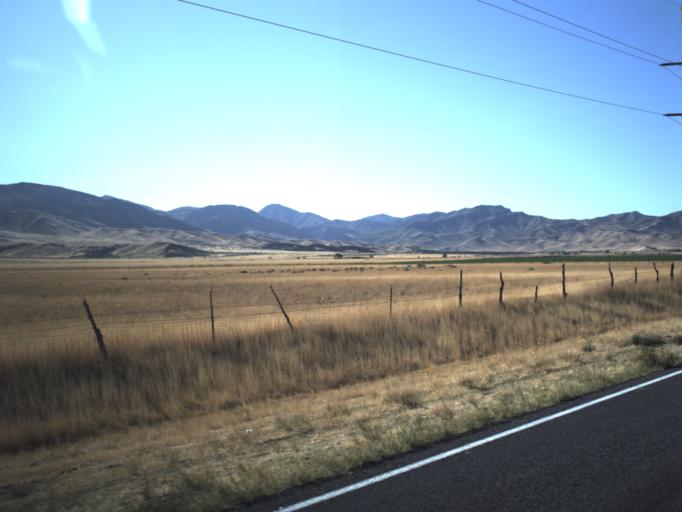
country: US
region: Utah
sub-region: Millard County
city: Delta
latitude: 39.4184
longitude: -112.3290
